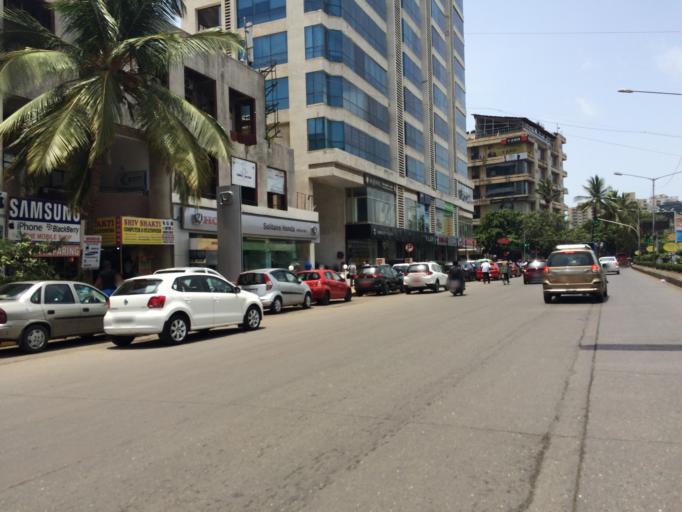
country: IN
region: Maharashtra
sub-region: Mumbai Suburban
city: Powai
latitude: 19.1361
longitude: 72.8320
